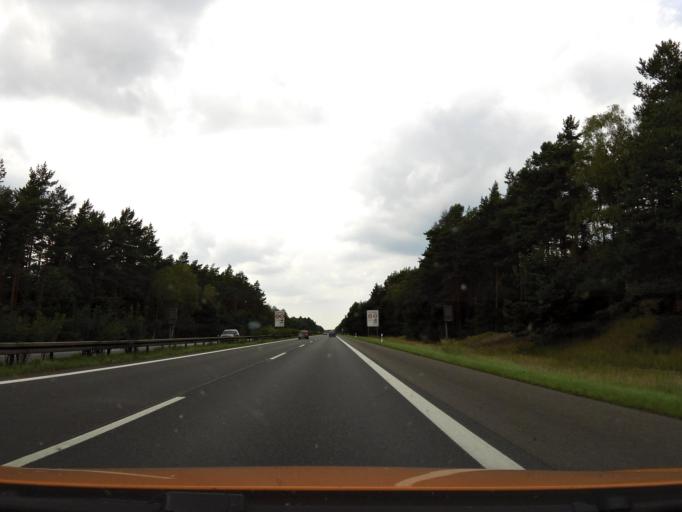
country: DE
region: Brandenburg
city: Birkenwerder
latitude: 52.6880
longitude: 13.3272
